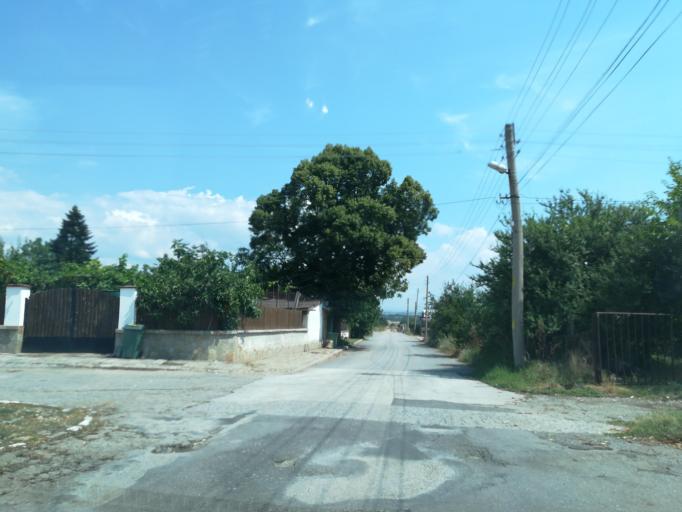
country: BG
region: Plovdiv
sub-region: Obshtina Asenovgrad
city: Asenovgrad
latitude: 41.9491
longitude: 24.9622
